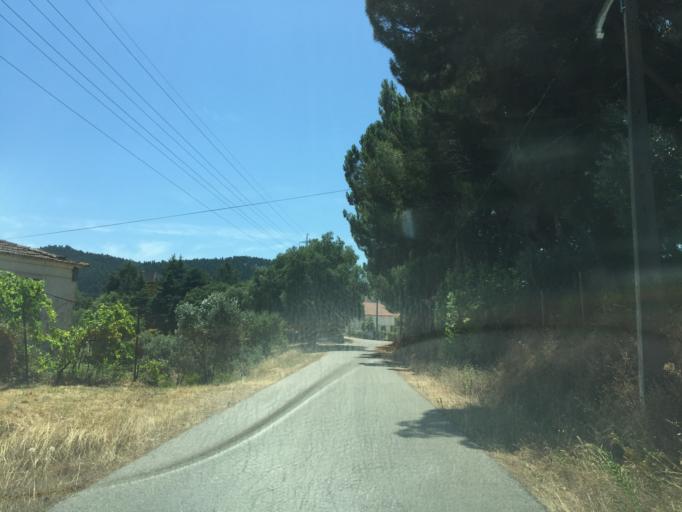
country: PT
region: Santarem
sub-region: Tomar
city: Tomar
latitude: 39.5923
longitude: -8.3488
